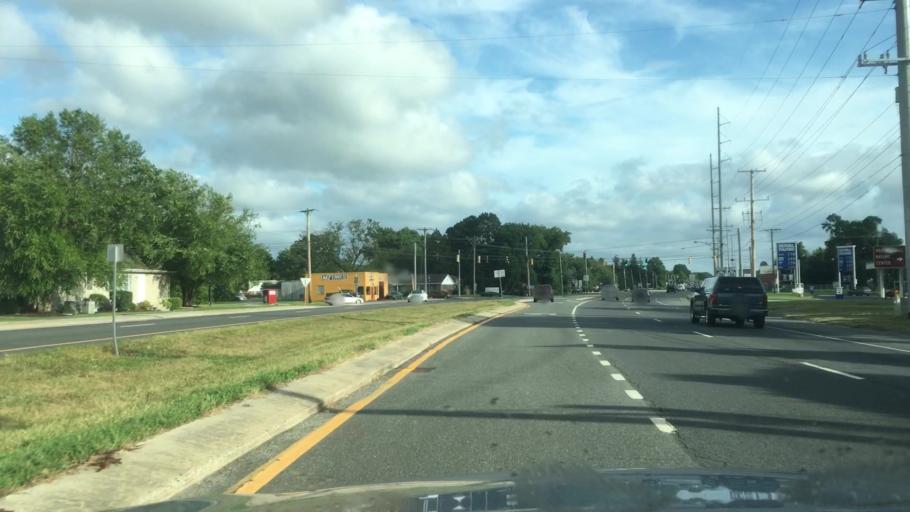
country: US
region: Delaware
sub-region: Sussex County
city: Milford
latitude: 38.9029
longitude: -75.4400
